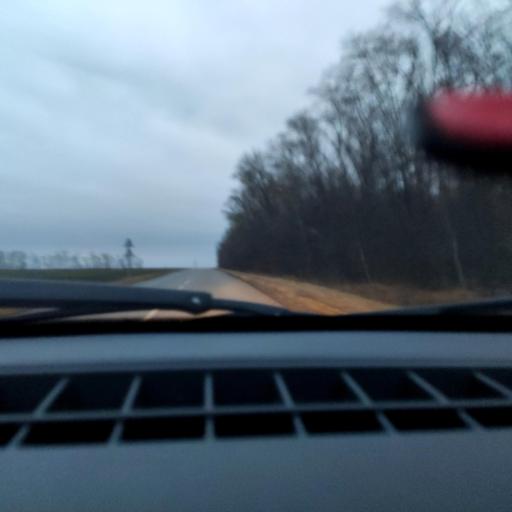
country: RU
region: Bashkortostan
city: Avdon
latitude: 54.5676
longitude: 55.6775
